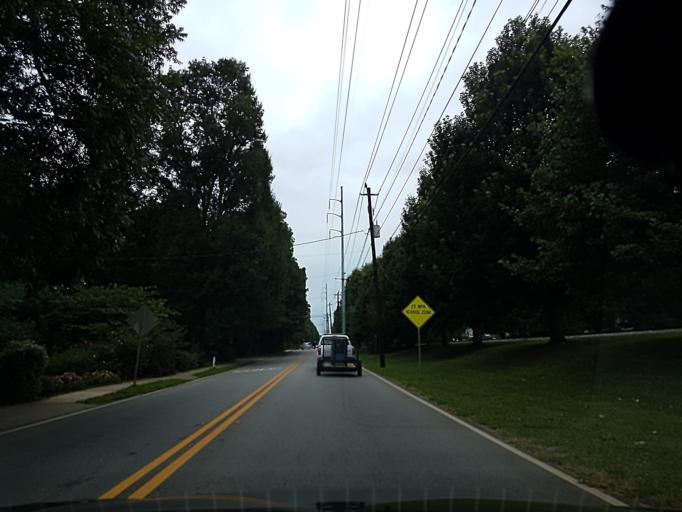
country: US
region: Georgia
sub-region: DeKalb County
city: Decatur
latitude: 33.7680
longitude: -84.3014
